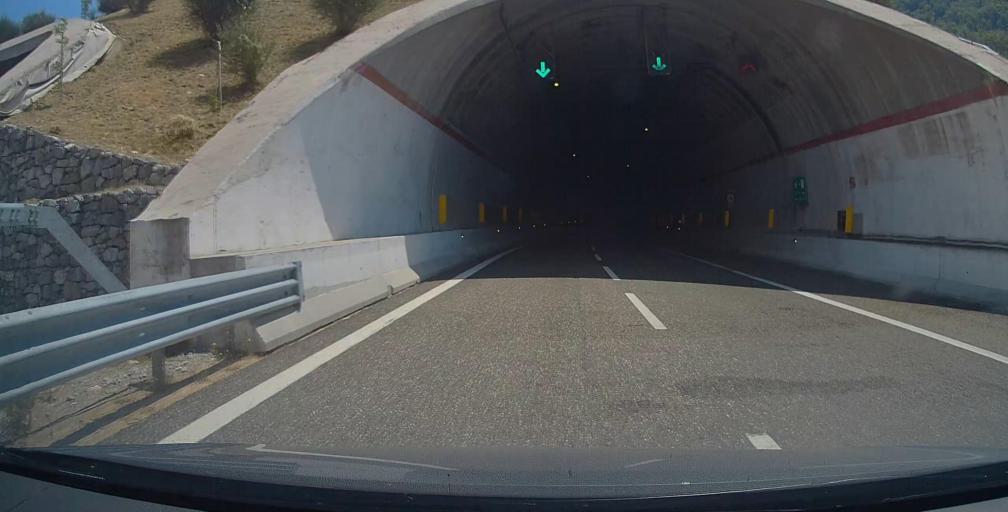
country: IT
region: Basilicate
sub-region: Provincia di Potenza
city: Lauria
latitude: 40.0707
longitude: 15.8675
